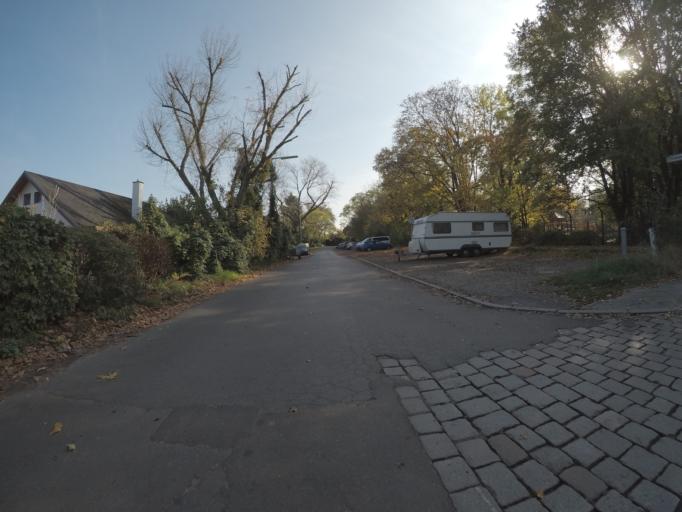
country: DE
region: Berlin
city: Buckow
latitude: 52.4412
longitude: 13.4747
